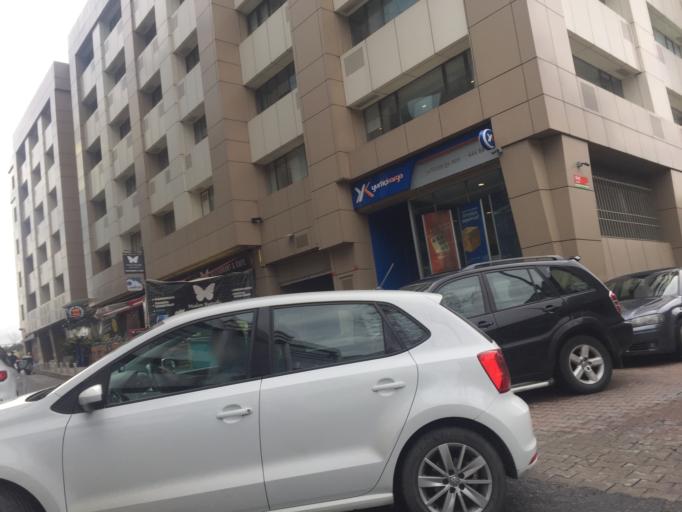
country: TR
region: Istanbul
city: Sisli
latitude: 41.0928
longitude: 29.0037
